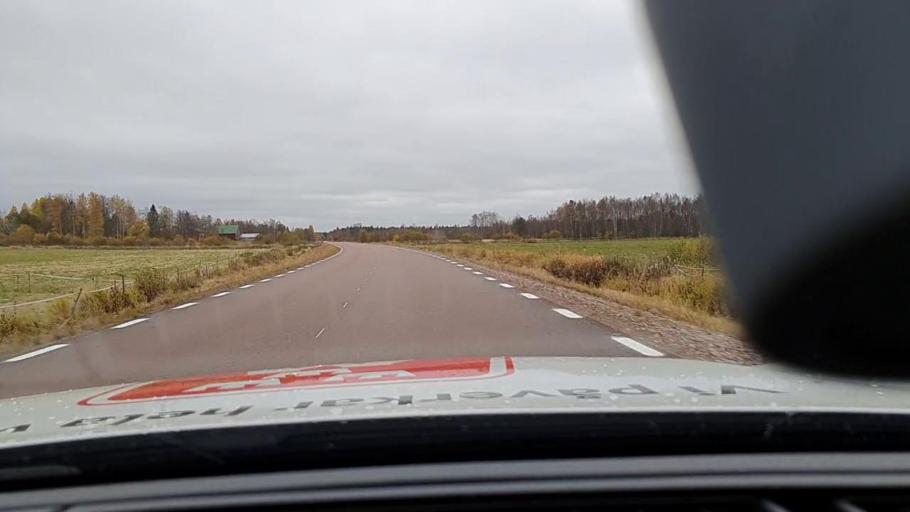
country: FI
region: Lapland
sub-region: Kemi-Tornio
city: Tornio
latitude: 66.0608
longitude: 23.9265
